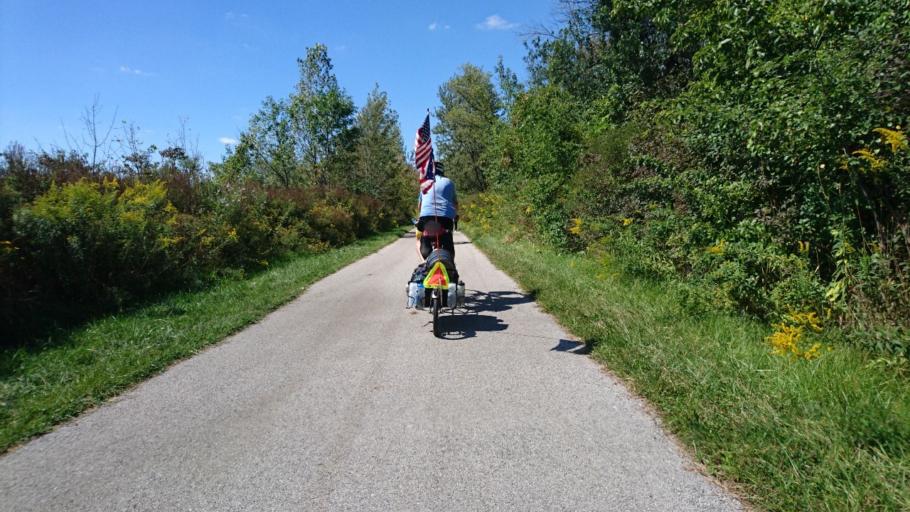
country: US
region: Illinois
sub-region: Cook County
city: Lansing
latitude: 41.5477
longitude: -87.5640
